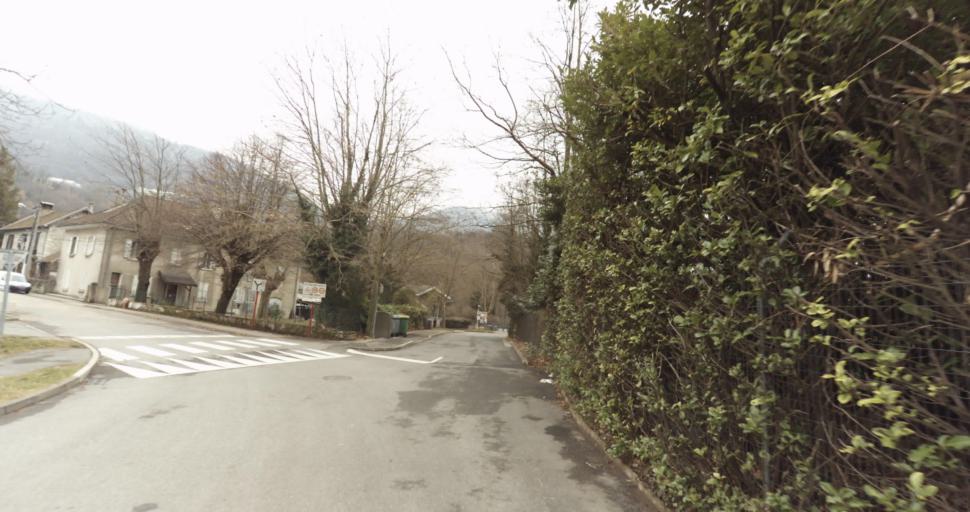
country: FR
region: Rhone-Alpes
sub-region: Departement de l'Isere
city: Le Gua
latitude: 45.0278
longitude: 5.6515
